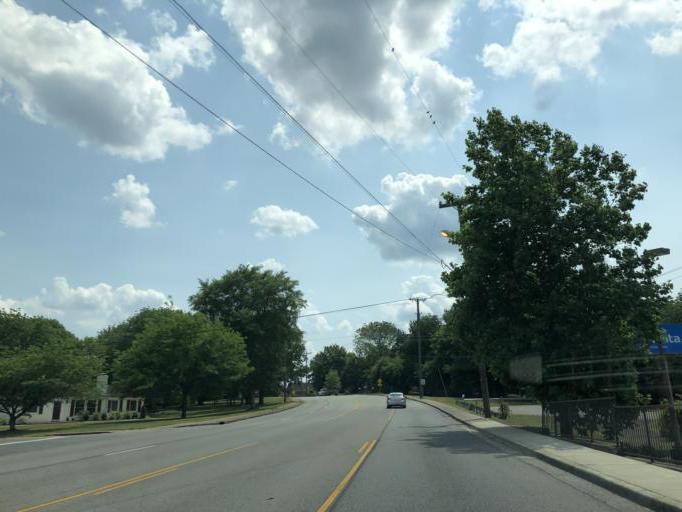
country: US
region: Tennessee
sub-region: Davidson County
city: Goodlettsville
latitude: 36.2467
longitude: -86.7353
